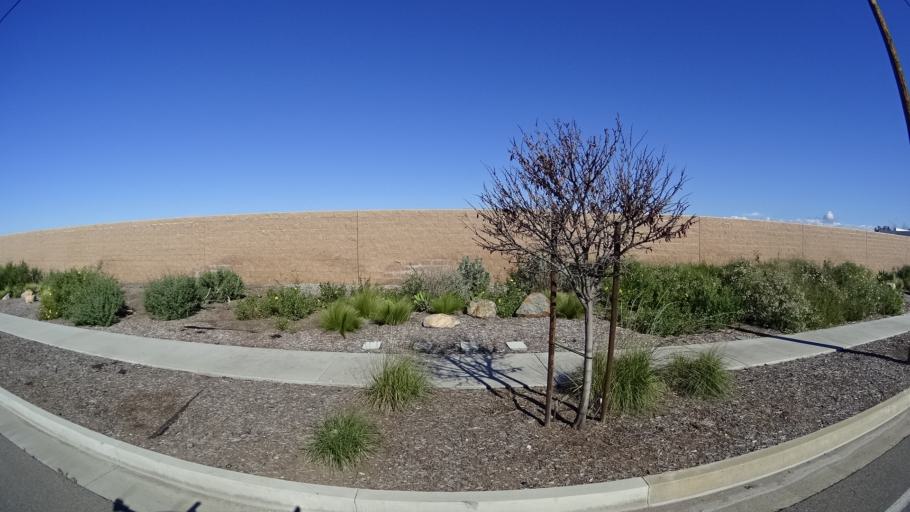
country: US
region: California
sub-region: Orange County
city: Placentia
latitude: 33.8598
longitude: -117.8533
